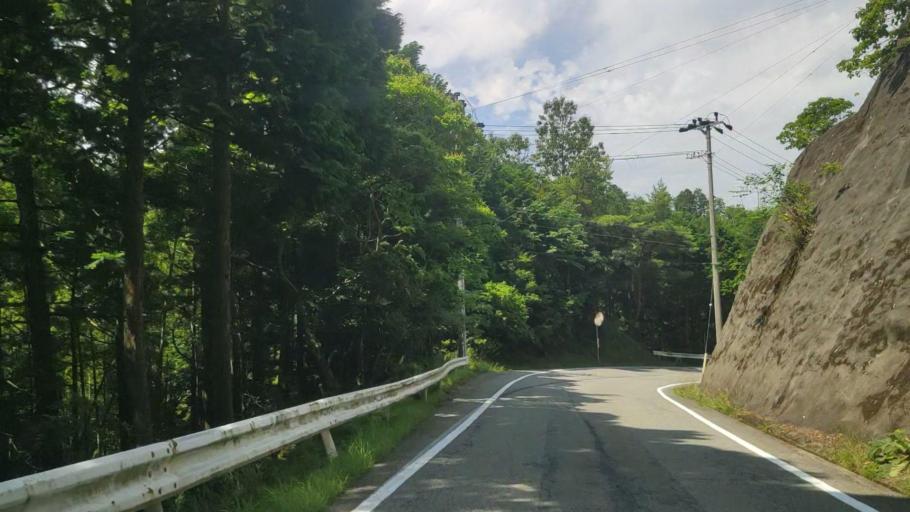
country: JP
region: Hyogo
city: Toyooka
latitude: 35.6398
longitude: 134.7678
